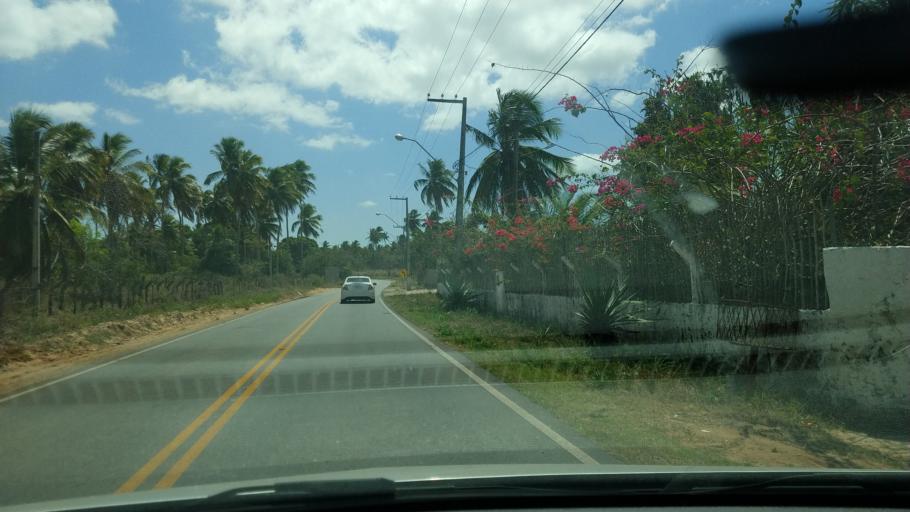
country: BR
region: Rio Grande do Norte
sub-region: Ares
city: Ares
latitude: -6.2292
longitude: -35.1429
